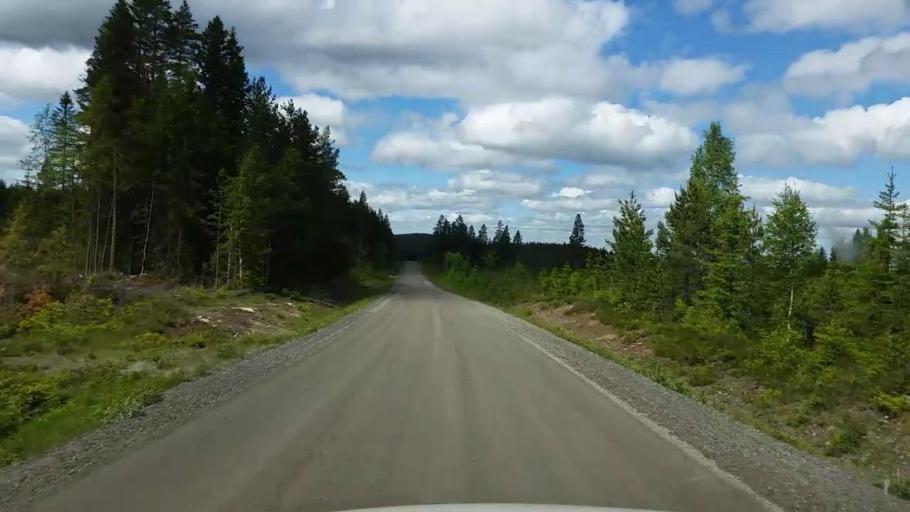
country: SE
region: Gaevleborg
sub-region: Bollnas Kommun
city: Vittsjo
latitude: 61.1786
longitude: 16.1466
